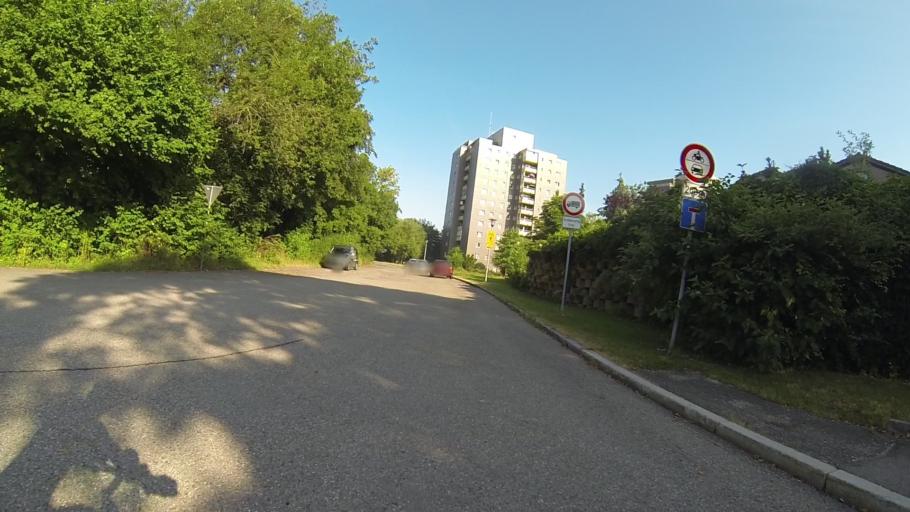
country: DE
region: Baden-Wuerttemberg
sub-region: Regierungsbezirk Stuttgart
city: Heidenheim an der Brenz
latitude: 48.6973
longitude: 10.1347
